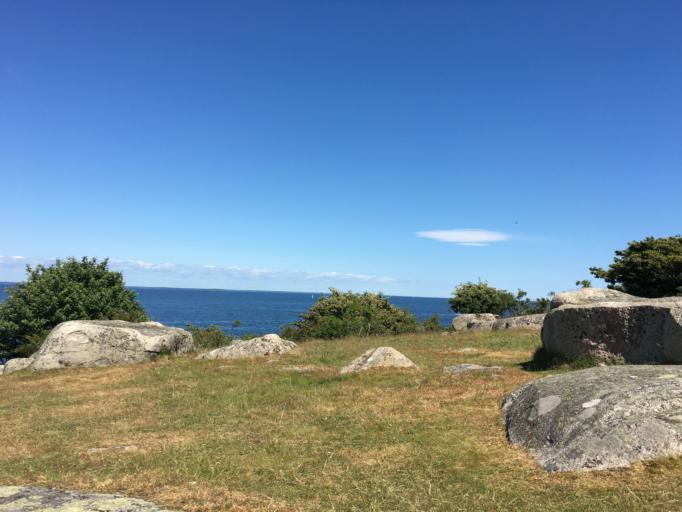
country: SE
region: Blekinge
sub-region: Karlshamns Kommun
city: Karlshamn
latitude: 56.0180
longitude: 14.8349
